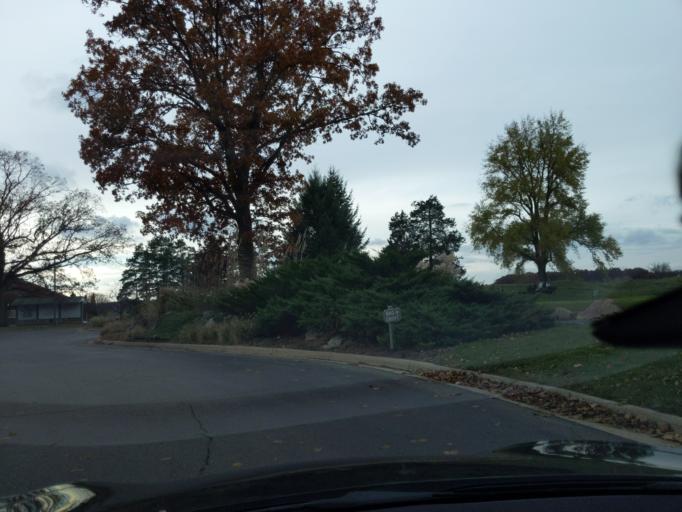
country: US
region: Michigan
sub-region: Clinton County
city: Bath
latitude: 42.7914
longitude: -84.4839
